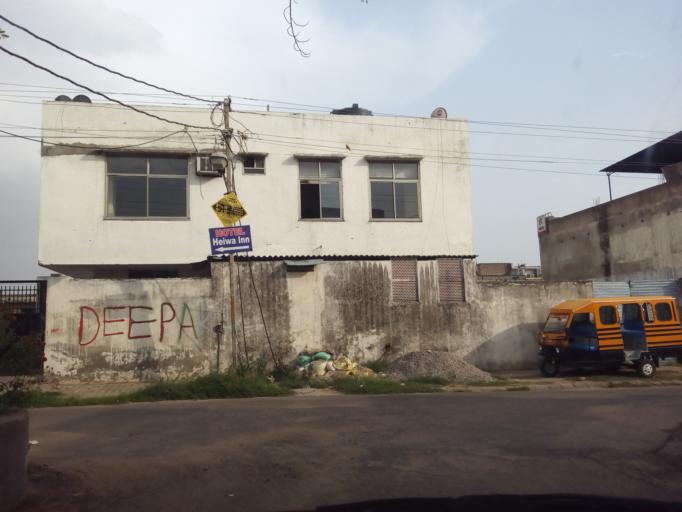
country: IN
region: Rajasthan
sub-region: Jaipur
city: Jaipur
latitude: 26.9157
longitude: 75.7957
